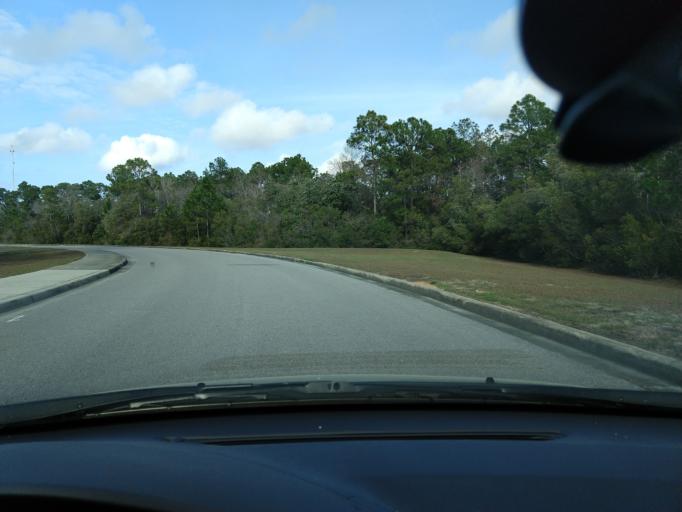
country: US
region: Florida
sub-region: Walton County
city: Seaside
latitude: 30.3716
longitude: -86.1816
